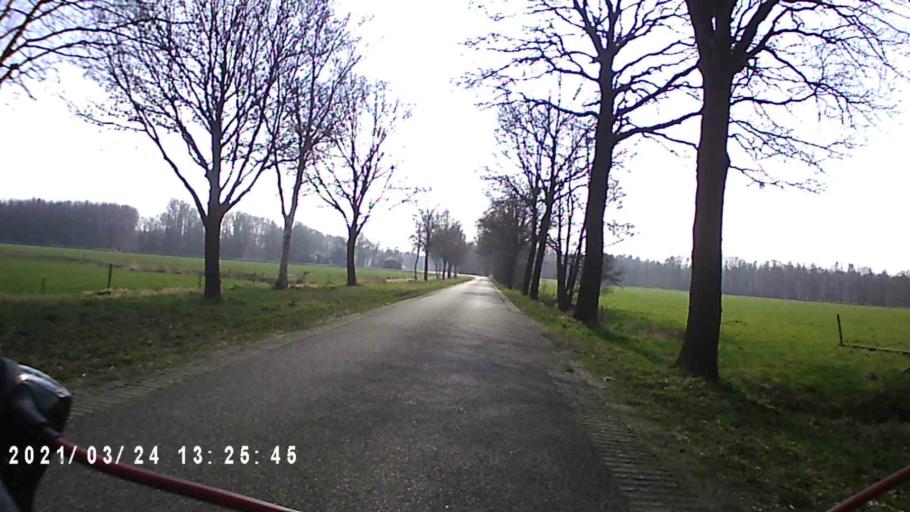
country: NL
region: Groningen
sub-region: Gemeente Leek
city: Leek
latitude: 53.0926
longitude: 6.2791
